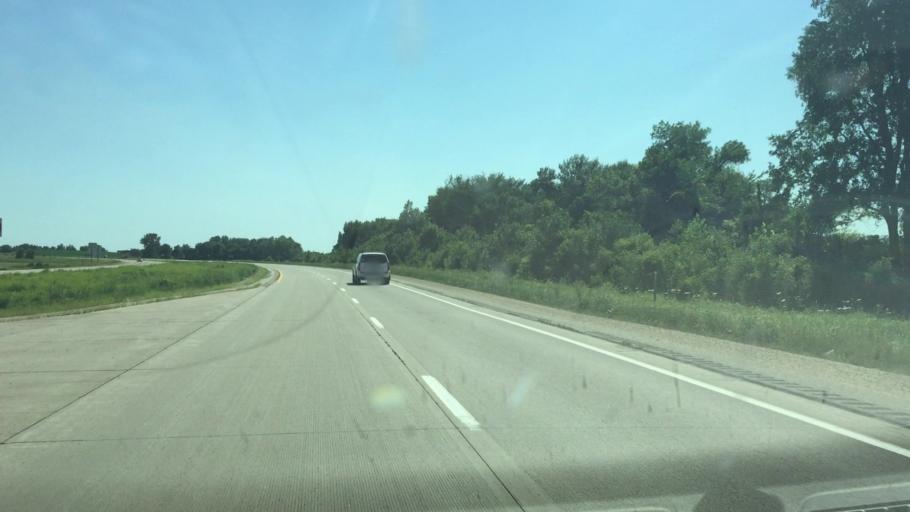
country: US
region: Iowa
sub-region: Jones County
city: Monticello
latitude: 42.1996
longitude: -91.2099
